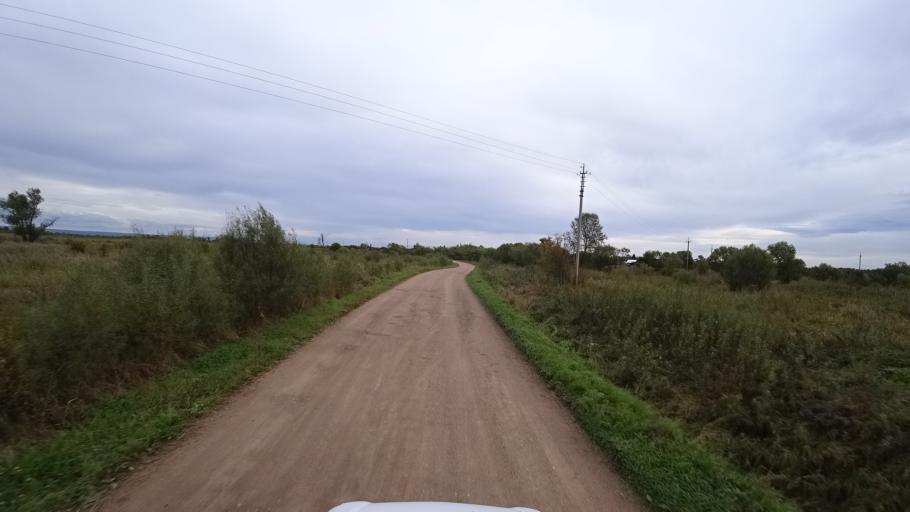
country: RU
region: Amur
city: Arkhara
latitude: 49.4366
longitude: 130.2610
